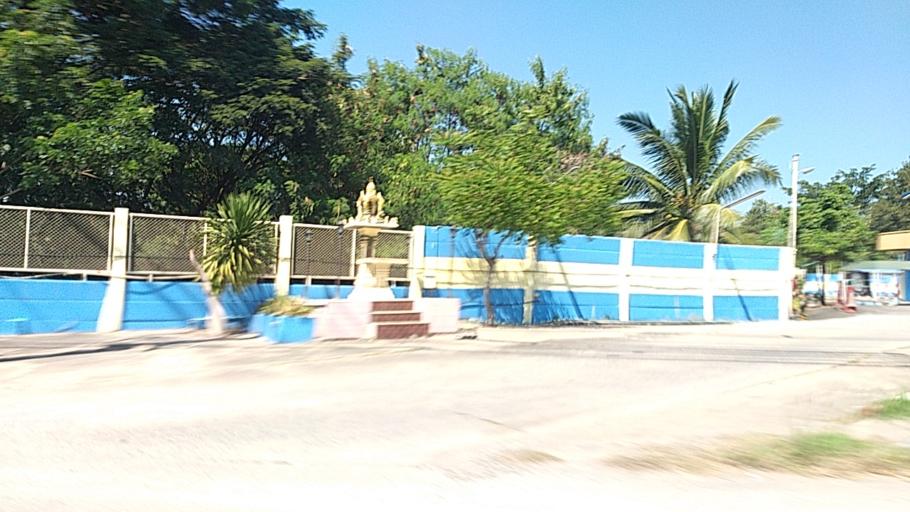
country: TH
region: Nakhon Ratchasima
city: Sung Noen
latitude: 14.8824
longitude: 101.8604
